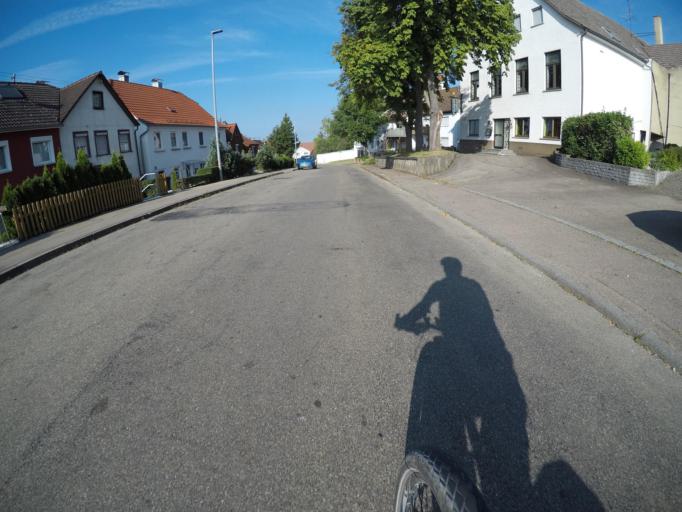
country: DE
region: Baden-Wuerttemberg
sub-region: Regierungsbezirk Stuttgart
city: Gerstetten
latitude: 48.6202
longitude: 10.0256
